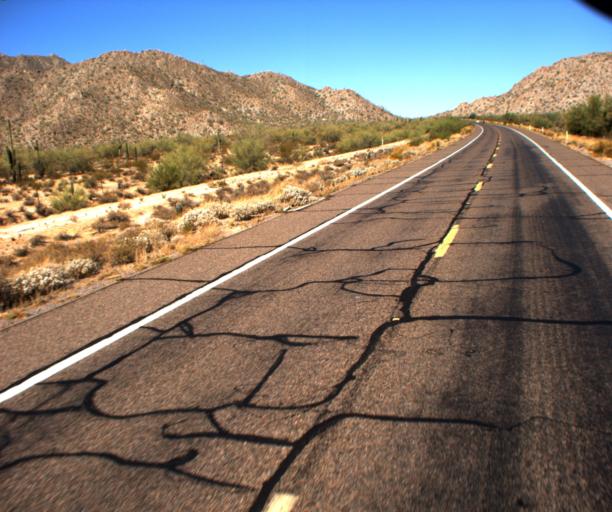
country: US
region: Arizona
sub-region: Pinal County
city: Blackwater
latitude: 33.0171
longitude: -111.6659
